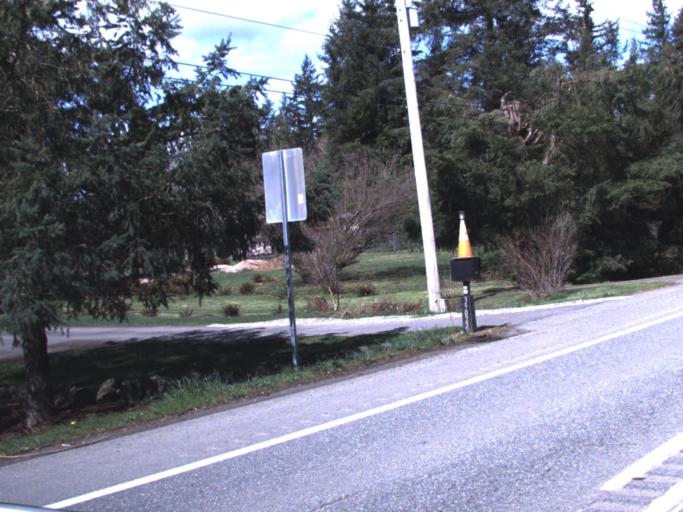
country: US
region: Washington
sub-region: King County
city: Enumclaw
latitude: 47.2512
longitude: -121.9900
